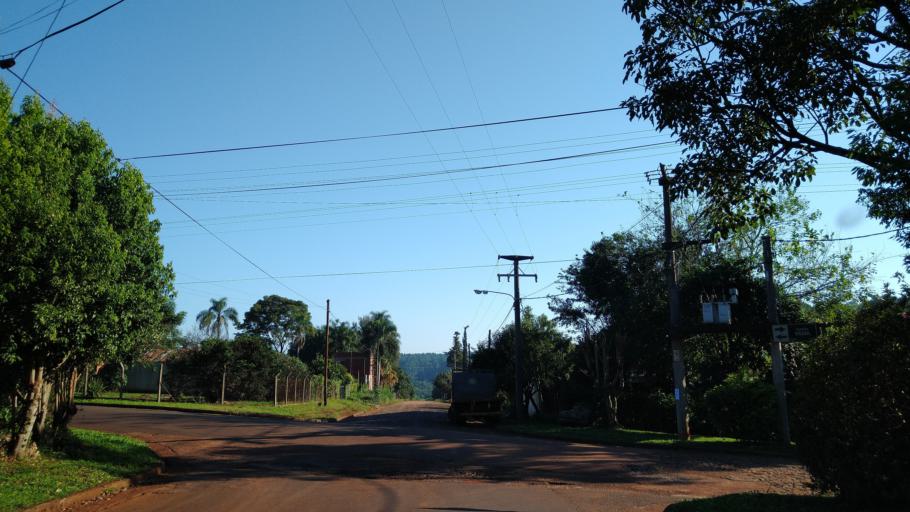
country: AR
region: Misiones
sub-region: Departamento de Montecarlo
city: Montecarlo
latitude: -26.5685
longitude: -54.7458
